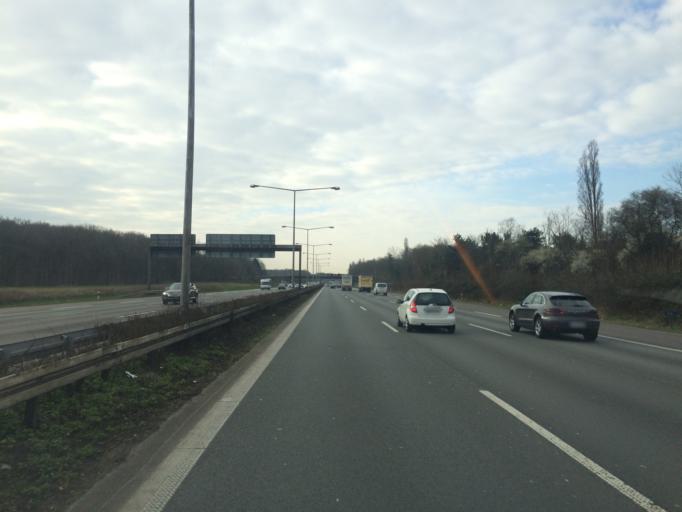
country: DE
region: North Rhine-Westphalia
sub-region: Regierungsbezirk Koln
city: Leverkusen
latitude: 51.0208
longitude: 7.0122
